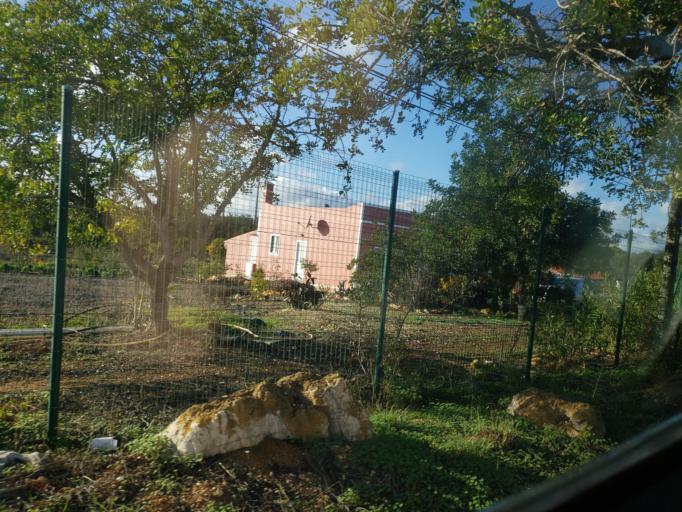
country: PT
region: Faro
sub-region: Portimao
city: Alvor
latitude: 37.1881
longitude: -8.5875
